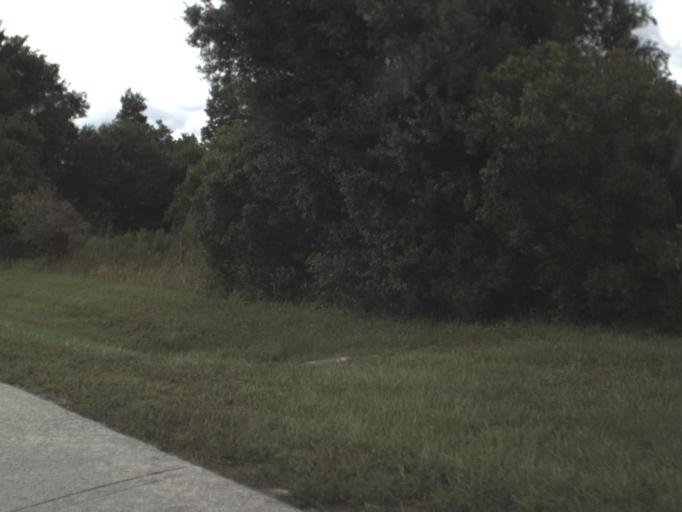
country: US
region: Florida
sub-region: DeSoto County
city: Nocatee
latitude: 27.2016
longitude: -81.9494
